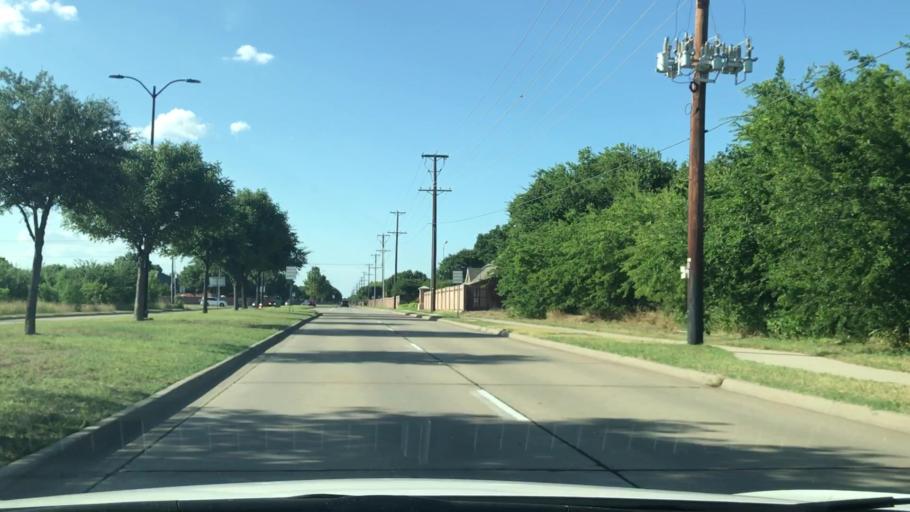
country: US
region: Texas
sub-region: Collin County
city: Frisco
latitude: 33.1074
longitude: -96.7882
